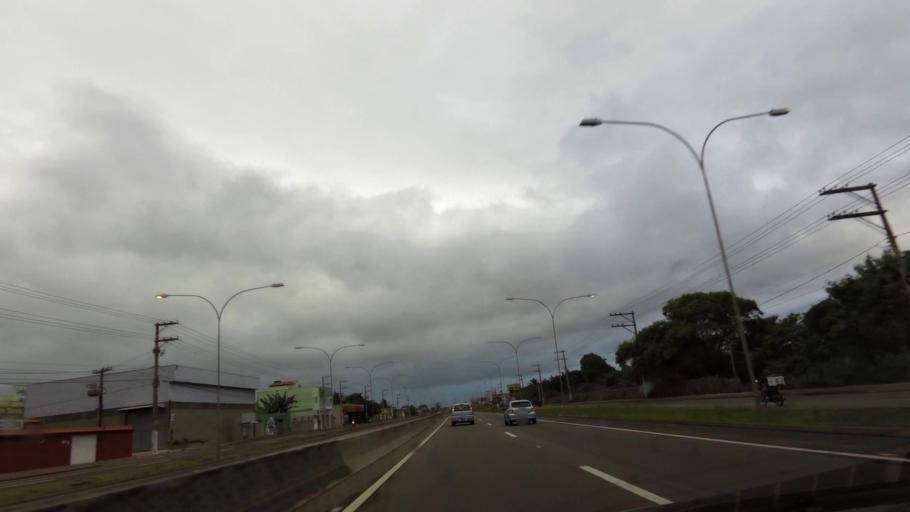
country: BR
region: Espirito Santo
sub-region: Vila Velha
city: Vila Velha
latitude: -20.4415
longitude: -40.3329
